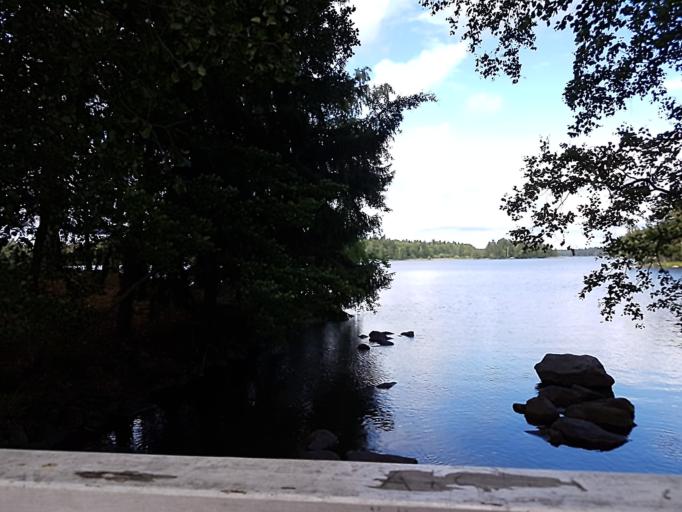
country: FI
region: Pirkanmaa
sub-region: Etelae-Pirkanmaa
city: Valkeakoski
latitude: 61.2722
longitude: 24.0484
